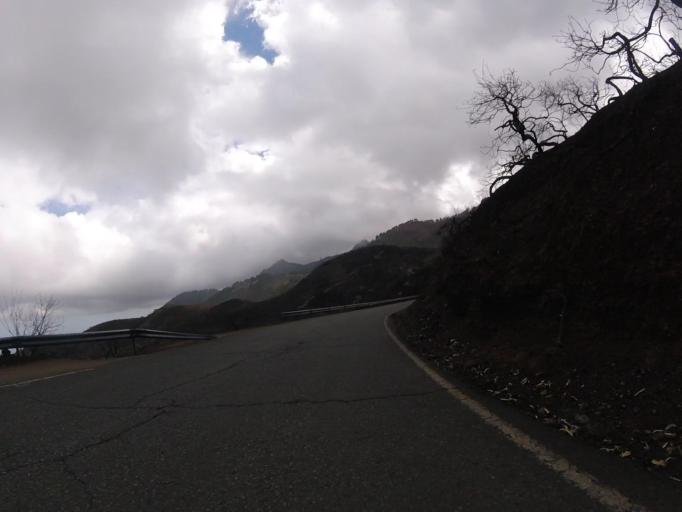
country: ES
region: Canary Islands
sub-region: Provincia de Las Palmas
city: Tejeda
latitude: 27.9846
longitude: -15.5728
